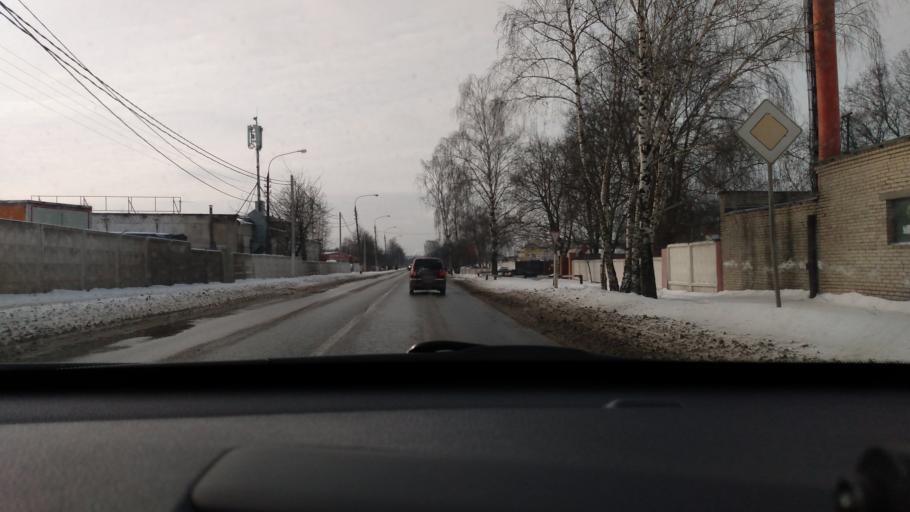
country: RU
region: Moskovskaya
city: Chornaya
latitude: 55.7587
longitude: 38.0736
